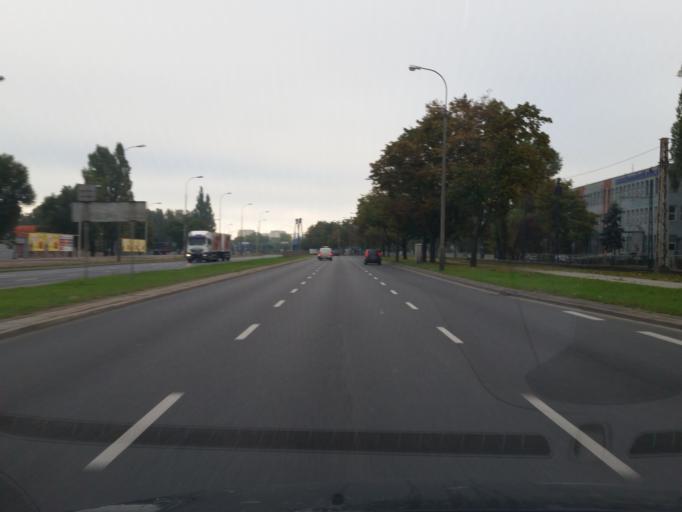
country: PL
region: Masovian Voivodeship
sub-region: Warszawa
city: Praga Polnoc
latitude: 52.2734
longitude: 21.0151
